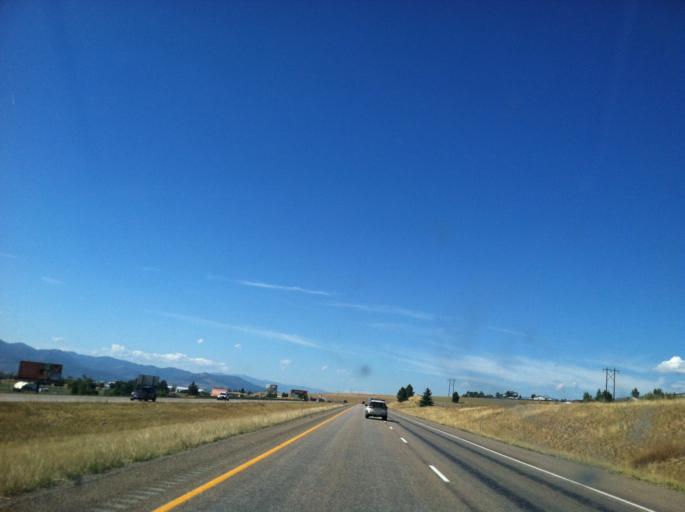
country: US
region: Montana
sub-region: Missoula County
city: Orchard Homes
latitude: 46.9317
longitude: -114.0846
